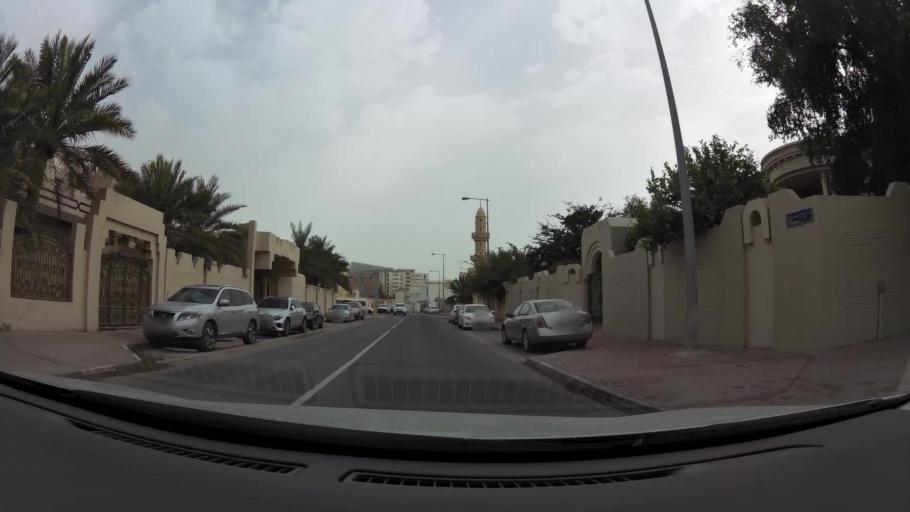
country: QA
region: Baladiyat ad Dawhah
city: Doha
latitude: 25.2642
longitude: 51.5489
